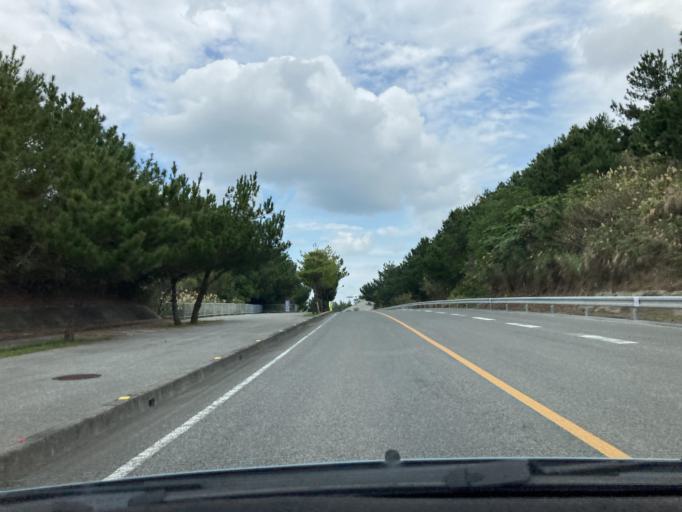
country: JP
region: Okinawa
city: Ishikawa
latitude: 26.4596
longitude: 127.8248
